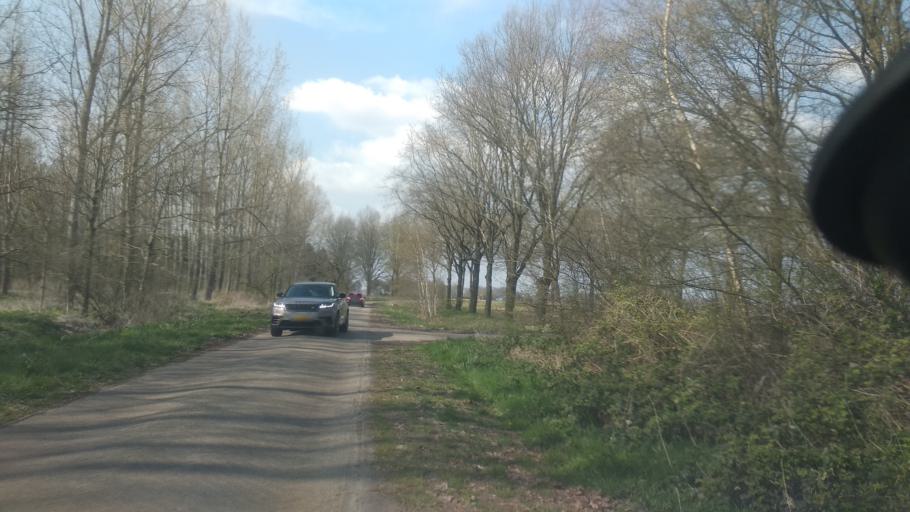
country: NL
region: Groningen
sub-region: Gemeente Stadskanaal
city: Stadskanaal
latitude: 52.9644
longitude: 6.8899
